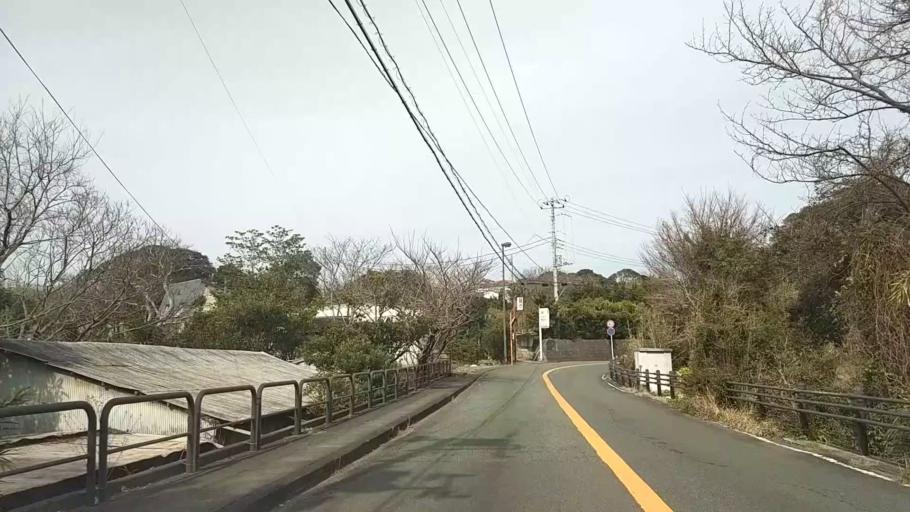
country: JP
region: Shizuoka
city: Shimoda
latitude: 34.6648
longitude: 138.9724
